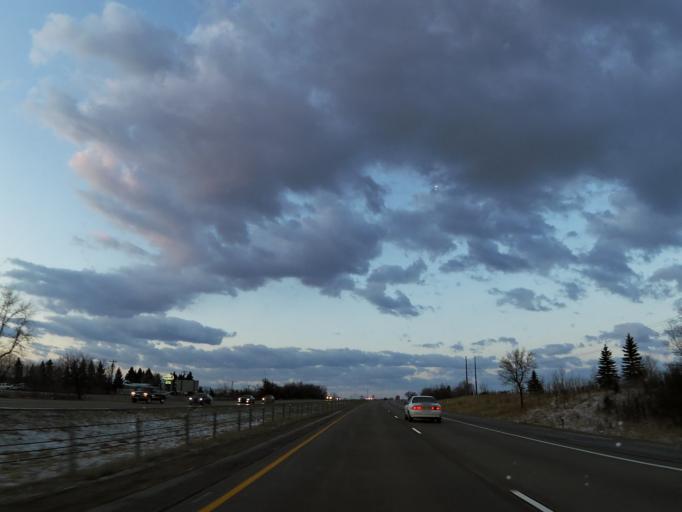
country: US
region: Minnesota
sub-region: Dakota County
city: Lakeville
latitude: 44.6584
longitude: -93.2941
